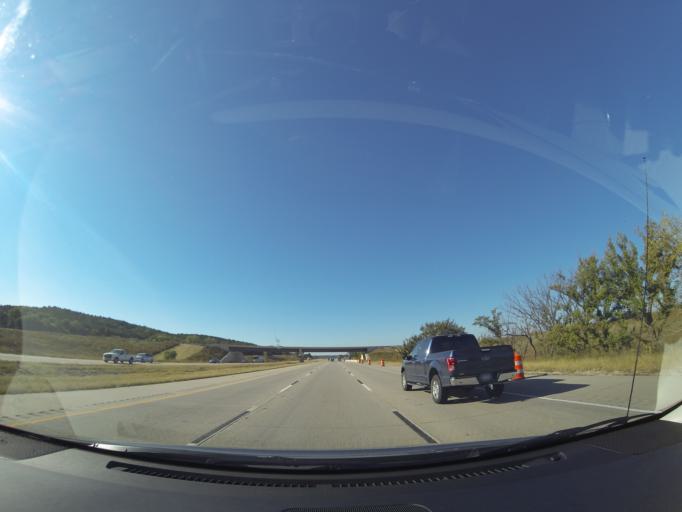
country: US
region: Nebraska
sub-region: Sarpy County
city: Gretna
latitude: 41.0732
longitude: -96.2845
